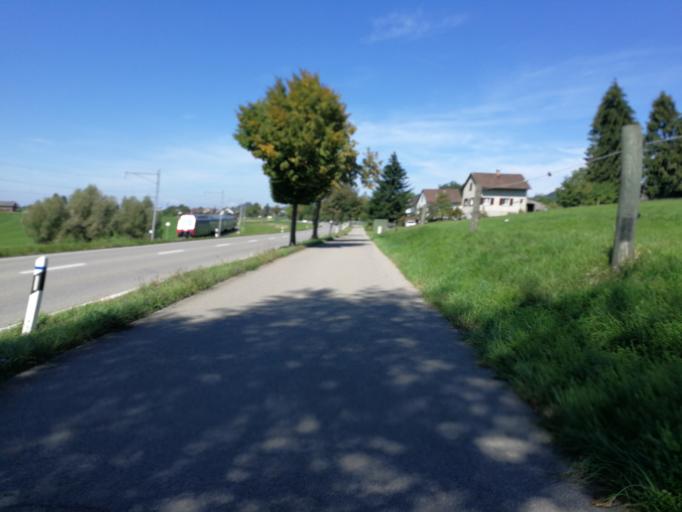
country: CH
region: Zurich
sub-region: Bezirk Pfaeffikon
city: Pfaeffikon / Irgenhausen
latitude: 47.3521
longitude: 8.8022
